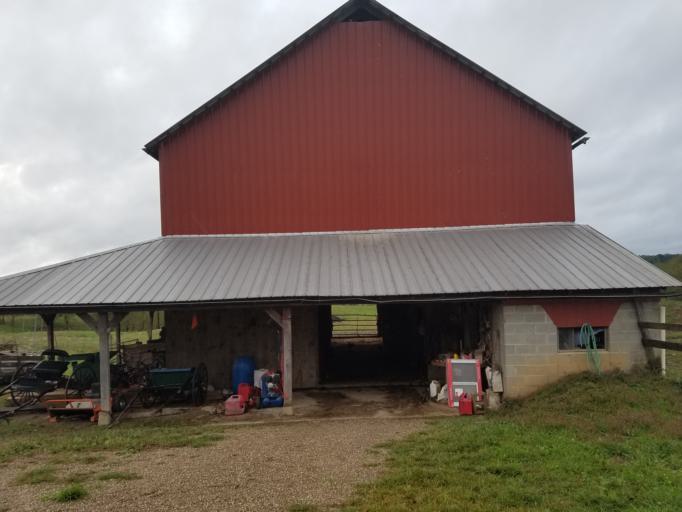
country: US
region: Ohio
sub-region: Belmont County
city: Barnesville
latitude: 40.0494
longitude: -81.3575
